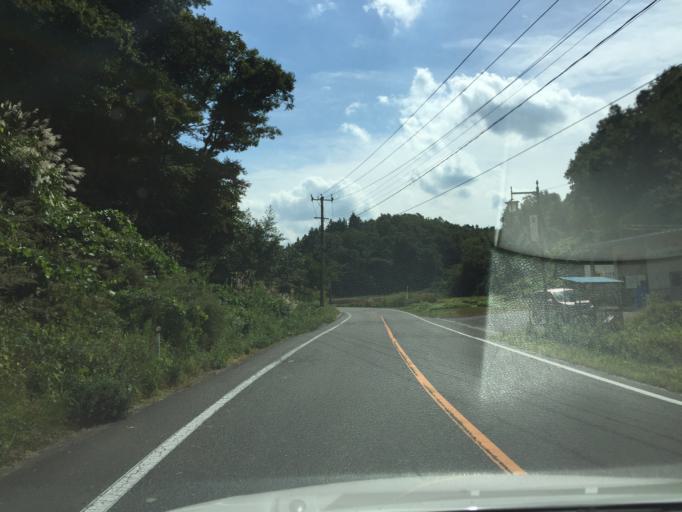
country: JP
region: Fukushima
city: Funehikimachi-funehiki
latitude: 37.4140
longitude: 140.5374
